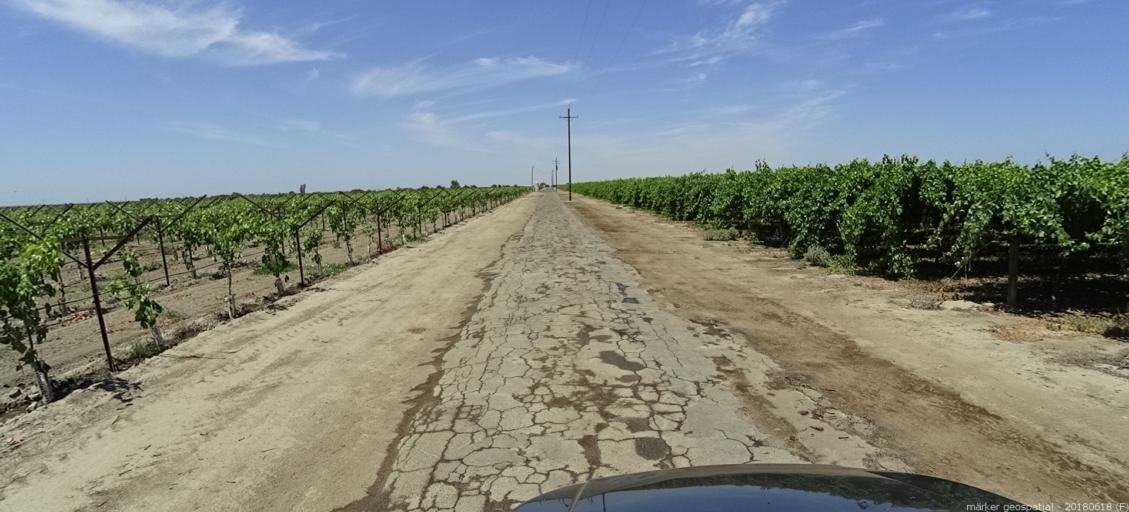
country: US
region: California
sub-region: Madera County
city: Parkwood
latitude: 36.8875
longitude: -120.1309
